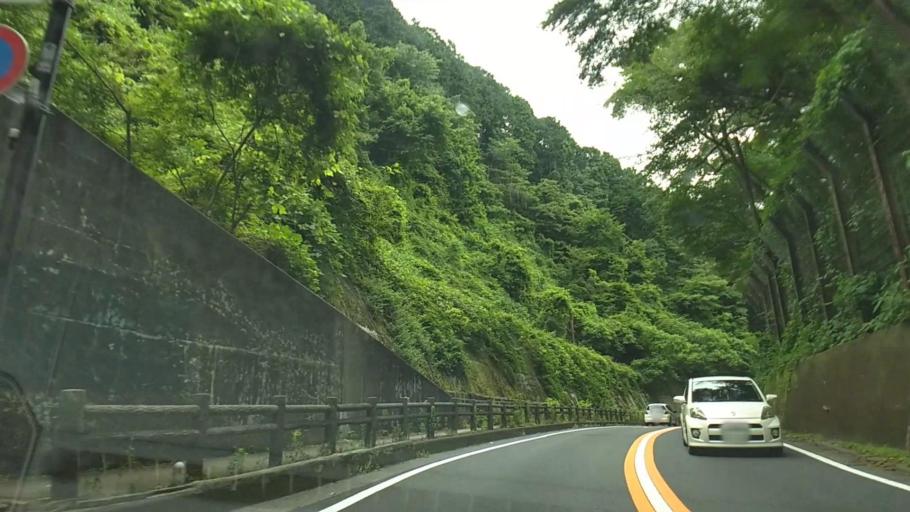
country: JP
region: Tokyo
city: Hachioji
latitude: 35.6214
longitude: 139.2282
